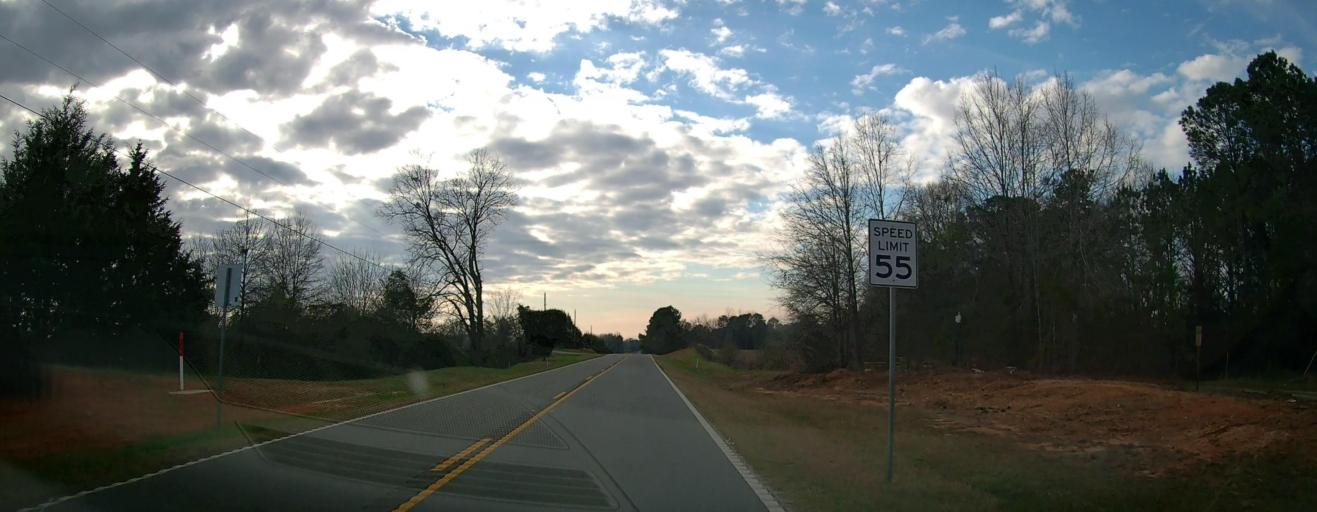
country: US
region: Georgia
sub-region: Harris County
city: Hamilton
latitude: 32.6837
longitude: -84.7549
